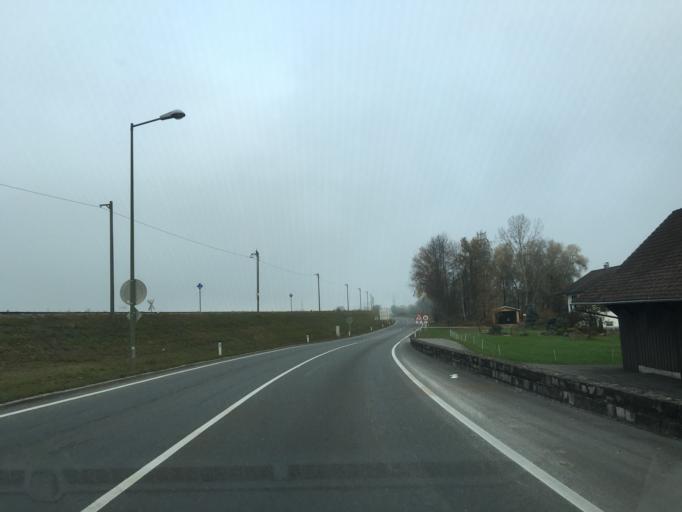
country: AT
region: Vorarlberg
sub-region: Politischer Bezirk Dornbirn
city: Lustenau
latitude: 47.4510
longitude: 9.6648
